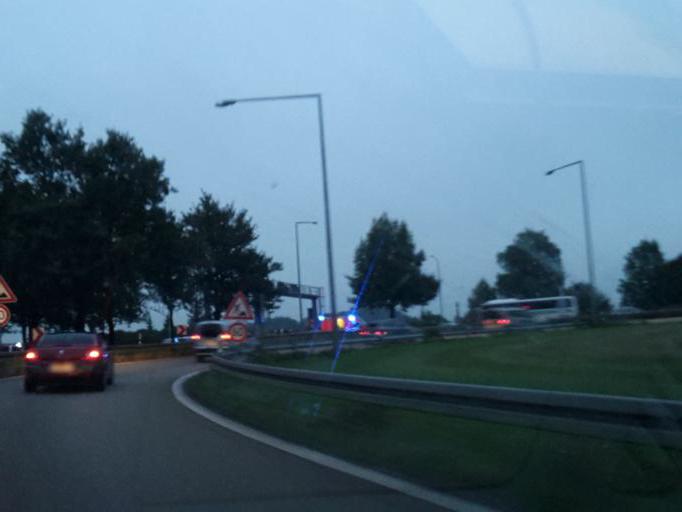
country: DE
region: North Rhine-Westphalia
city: Opladen
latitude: 51.0426
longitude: 7.0054
